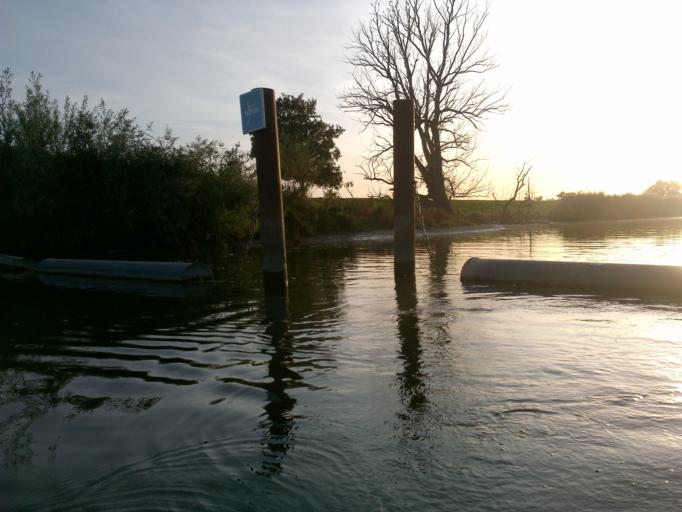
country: NL
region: South Holland
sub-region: Gemeente Sliedrecht
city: Sliedrecht
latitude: 51.7635
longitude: 4.7632
